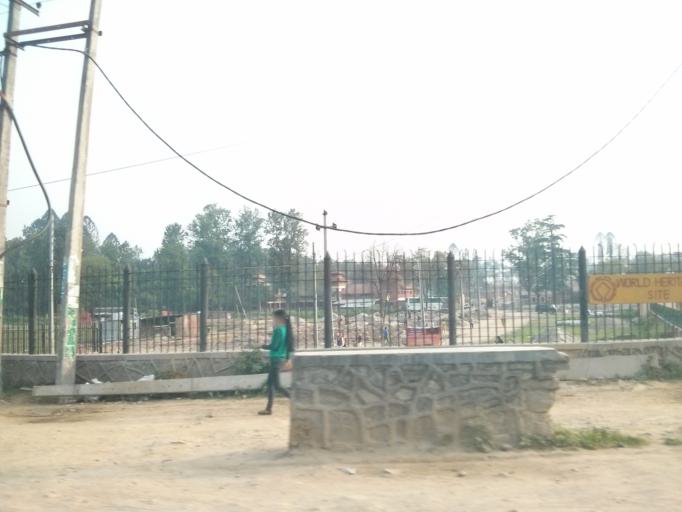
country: NP
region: Central Region
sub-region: Bagmati Zone
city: Kathmandu
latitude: 27.7058
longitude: 85.3475
